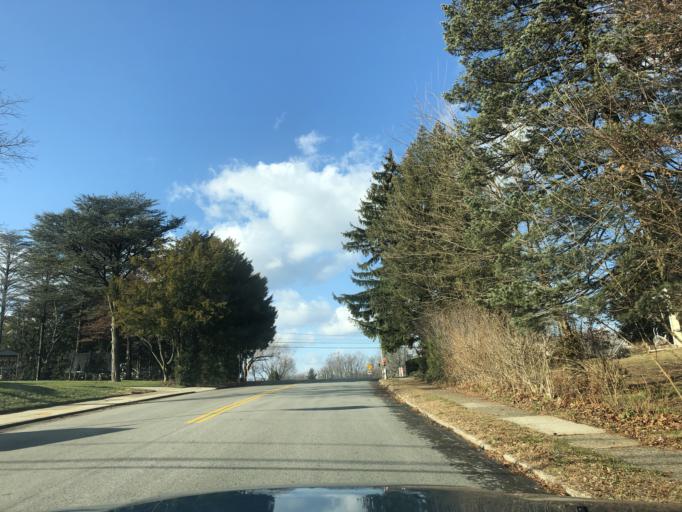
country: US
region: Pennsylvania
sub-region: Delaware County
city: Broomall
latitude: 39.9712
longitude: -75.3432
